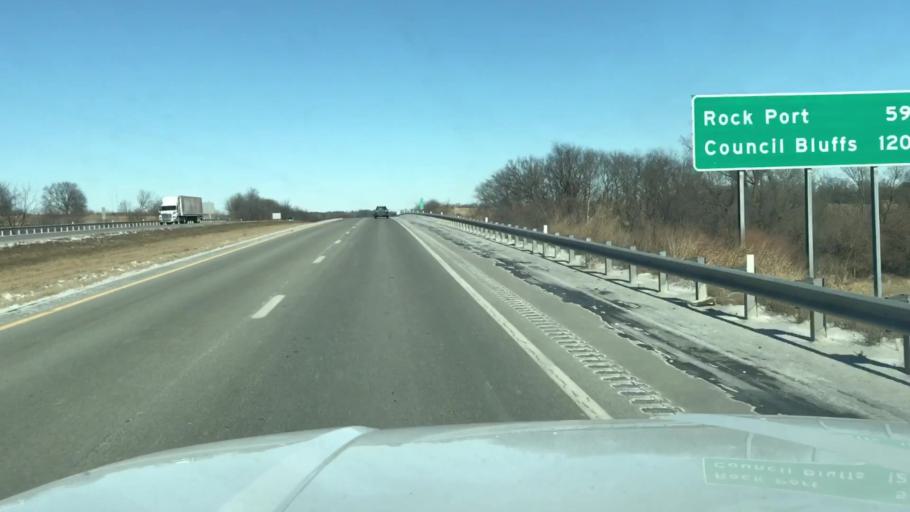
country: US
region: Missouri
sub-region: Andrew County
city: Country Club Village
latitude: 39.8278
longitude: -94.8052
